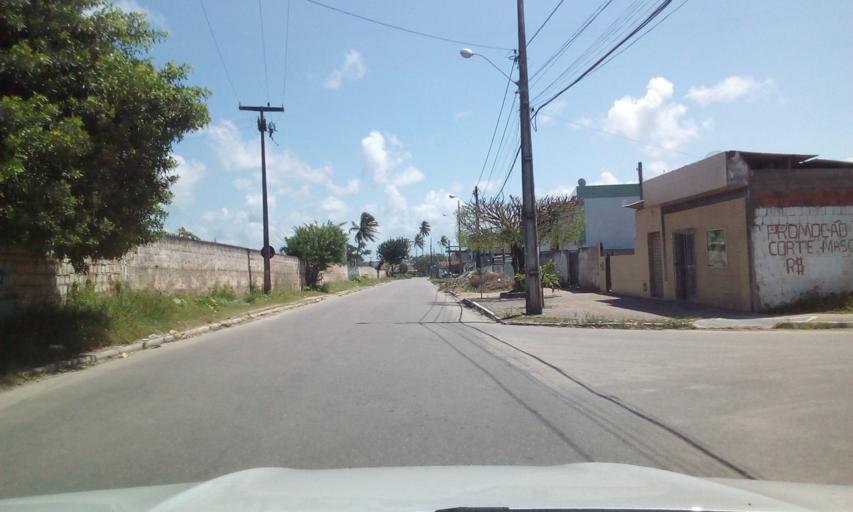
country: BR
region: Paraiba
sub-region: Conde
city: Conde
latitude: -7.2067
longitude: -34.8315
